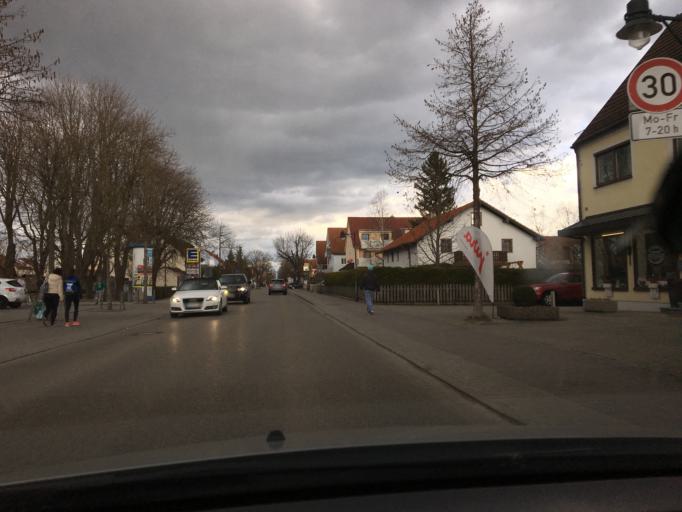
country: DE
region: Bavaria
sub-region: Upper Bavaria
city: Hallbergmoos
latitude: 48.3188
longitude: 11.7458
